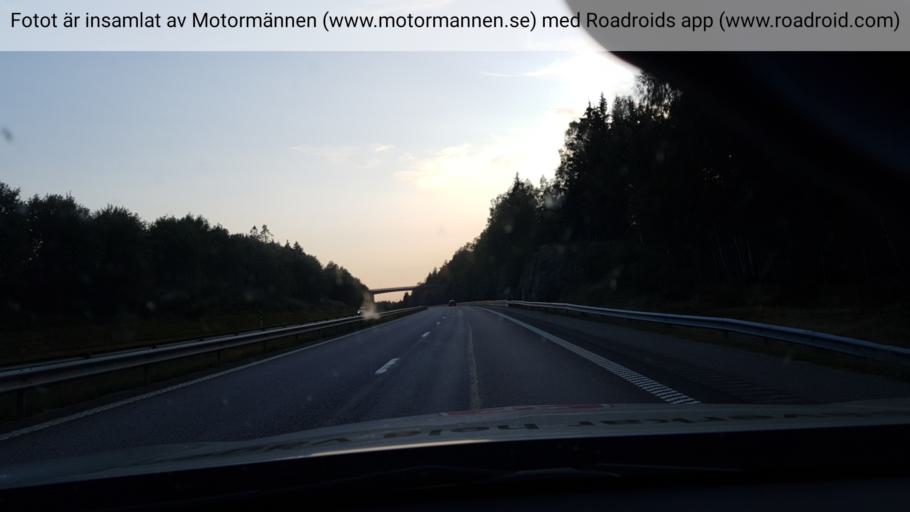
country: SE
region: Vaestra Goetaland
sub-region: Boras Kommun
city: Sandared
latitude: 57.6810
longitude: 12.7226
